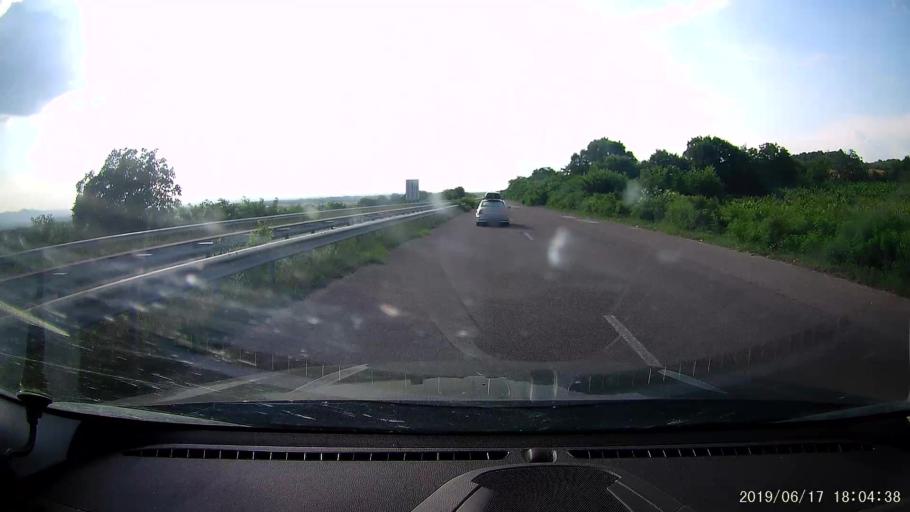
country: BG
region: Khaskovo
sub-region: Obshtina Svilengrad
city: Svilengrad
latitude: 41.7879
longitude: 26.1941
